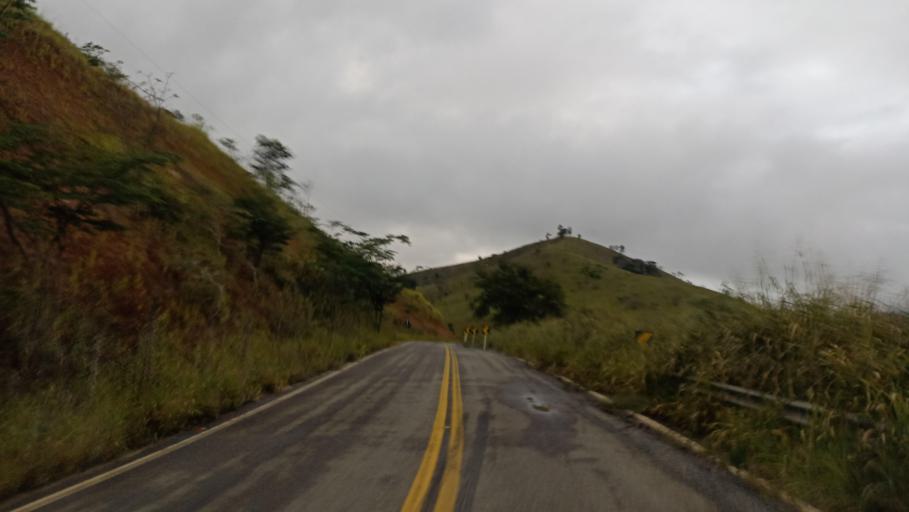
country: BR
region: Minas Gerais
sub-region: Joaima
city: Joaima
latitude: -16.6899
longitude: -40.5213
